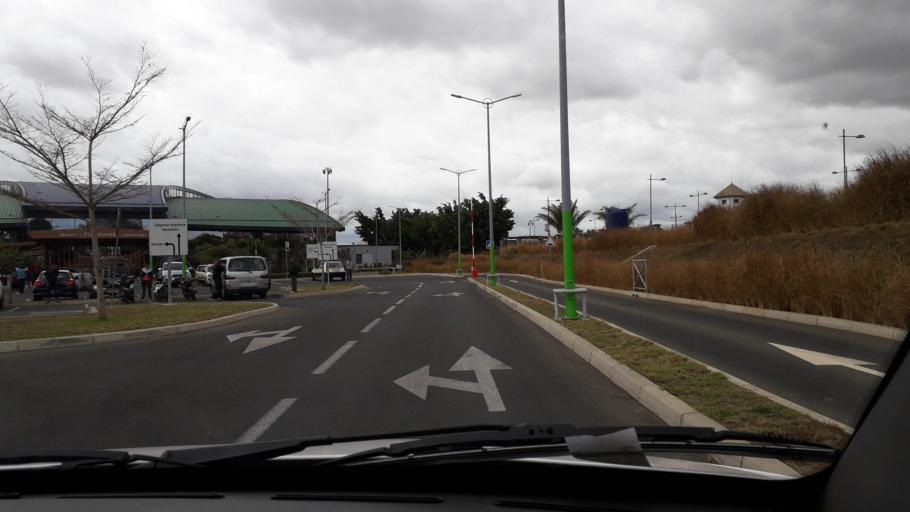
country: MG
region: Analamanga
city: Antananarivo
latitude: -18.8019
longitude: 47.4796
